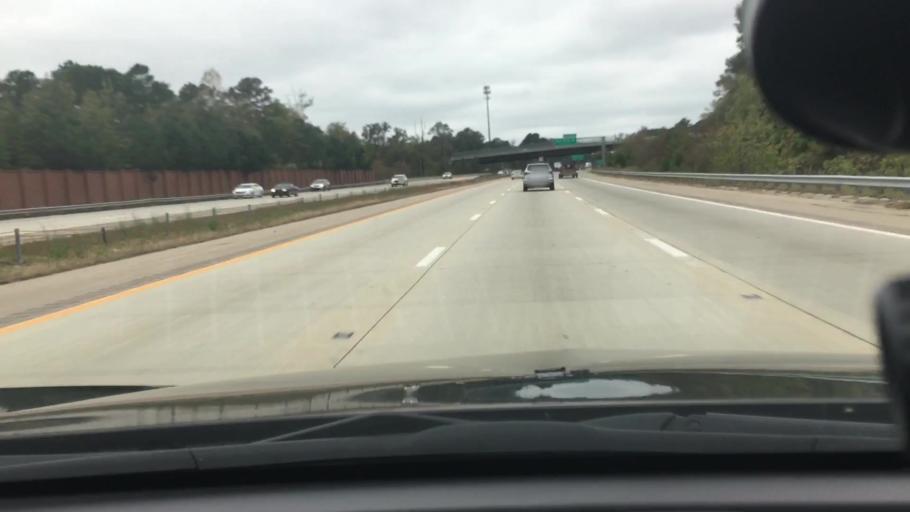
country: US
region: North Carolina
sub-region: Wake County
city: Knightdale
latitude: 35.7733
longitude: -78.5451
